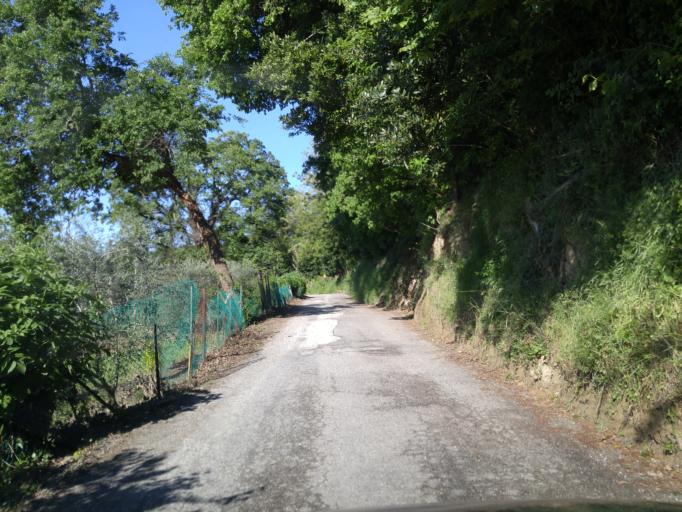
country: IT
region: The Marches
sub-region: Provincia di Pesaro e Urbino
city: Mombaroccio
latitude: 43.7972
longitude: 12.8627
